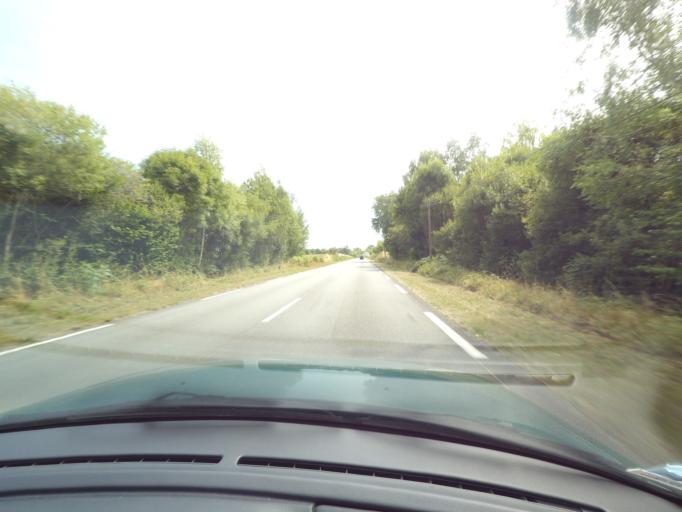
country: FR
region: Limousin
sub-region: Departement de la Haute-Vienne
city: Saint-Paul
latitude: 45.7975
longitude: 1.4143
